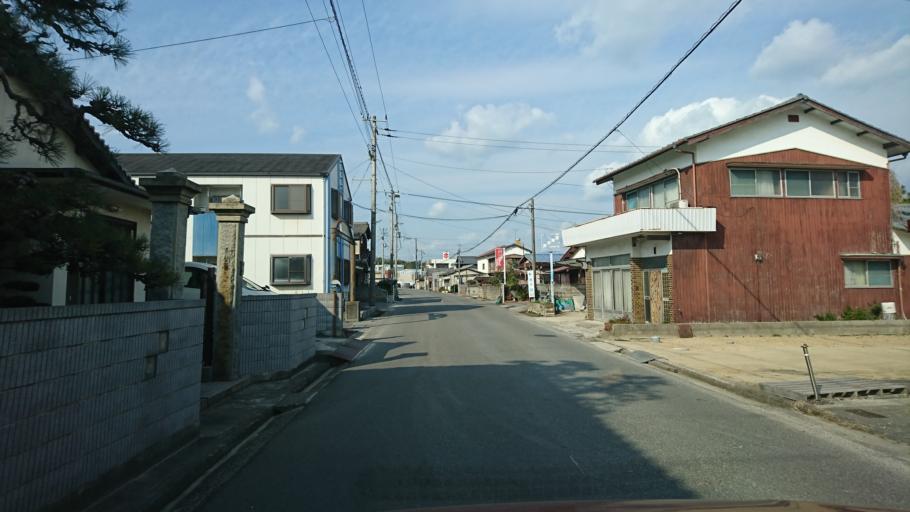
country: JP
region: Ehime
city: Saijo
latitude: 34.0235
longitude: 133.0390
